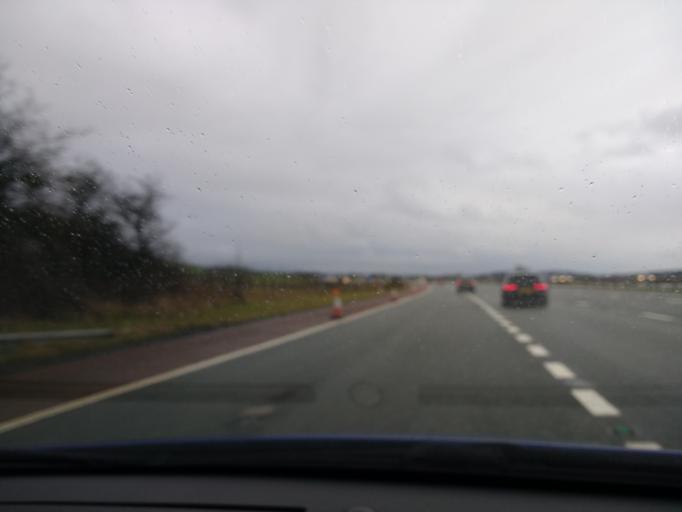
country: GB
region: England
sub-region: Cumbria
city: Milnthorpe
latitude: 54.2324
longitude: -2.7200
